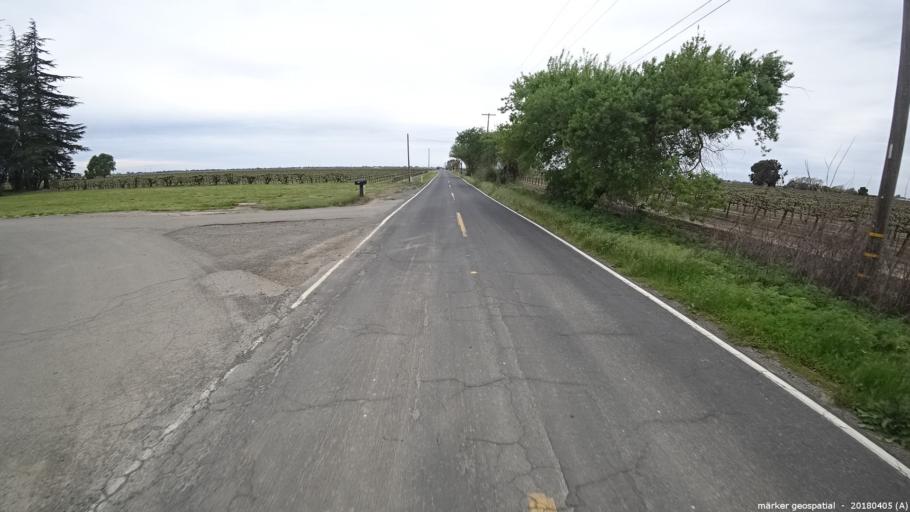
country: US
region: California
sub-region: Sacramento County
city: Walnut Grove
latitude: 38.3206
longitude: -121.5225
